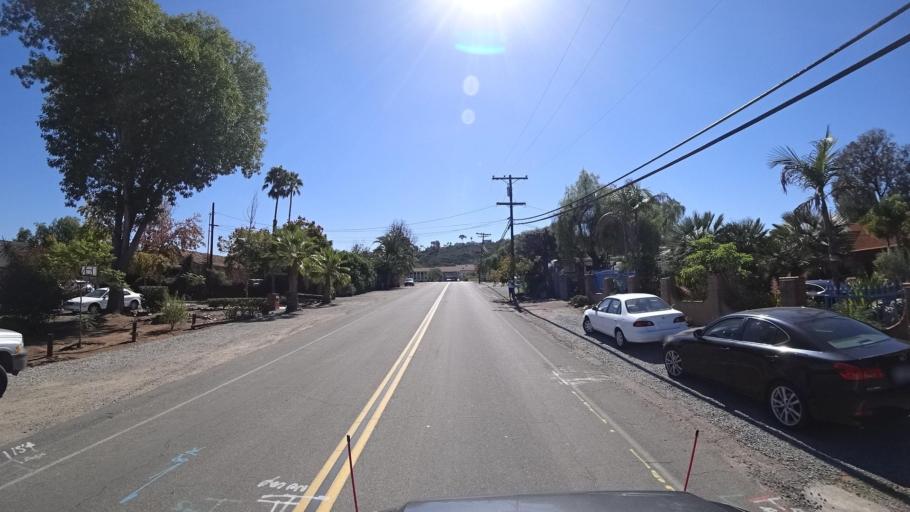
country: US
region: California
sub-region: San Diego County
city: Bonita
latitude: 32.6577
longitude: -117.0340
